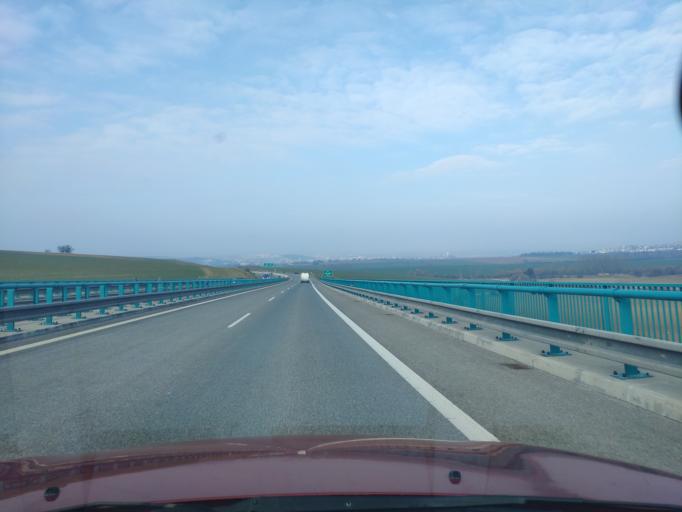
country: SK
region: Nitriansky
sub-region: Okres Nitra
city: Nitra
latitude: 48.3158
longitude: 18.1569
